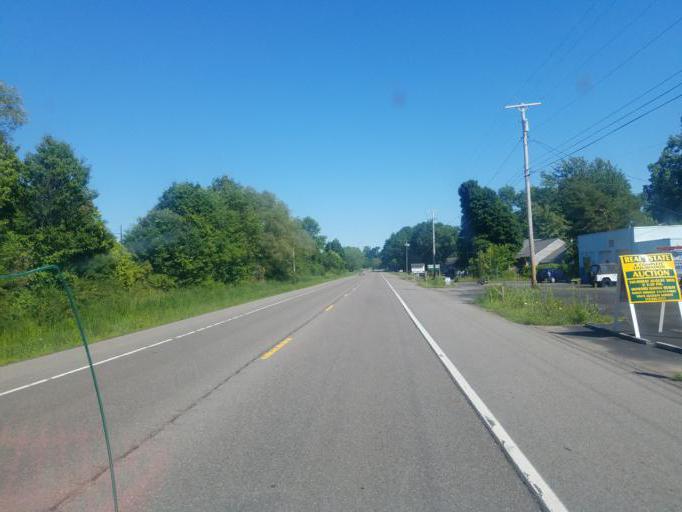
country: US
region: New York
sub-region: Wayne County
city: Lyons
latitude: 43.0627
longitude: -77.0216
